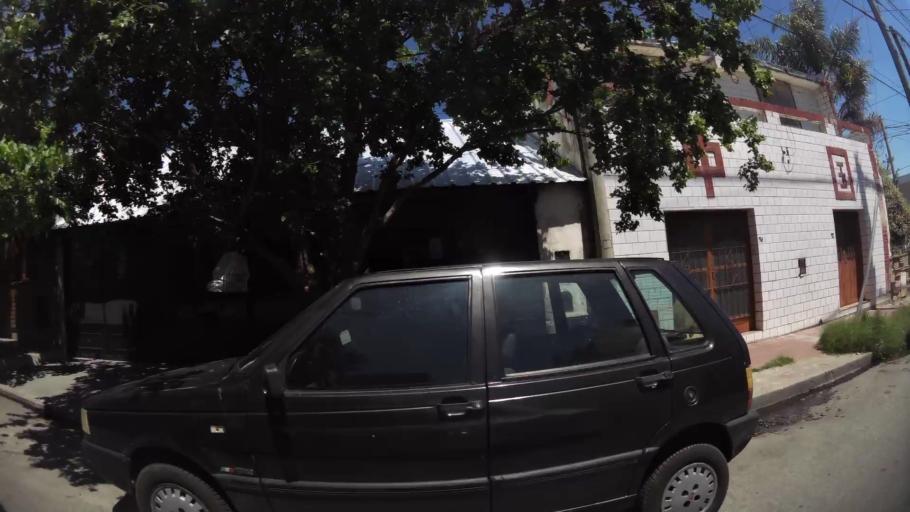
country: AR
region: Cordoba
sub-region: Departamento de Capital
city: Cordoba
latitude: -31.3940
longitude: -64.2005
